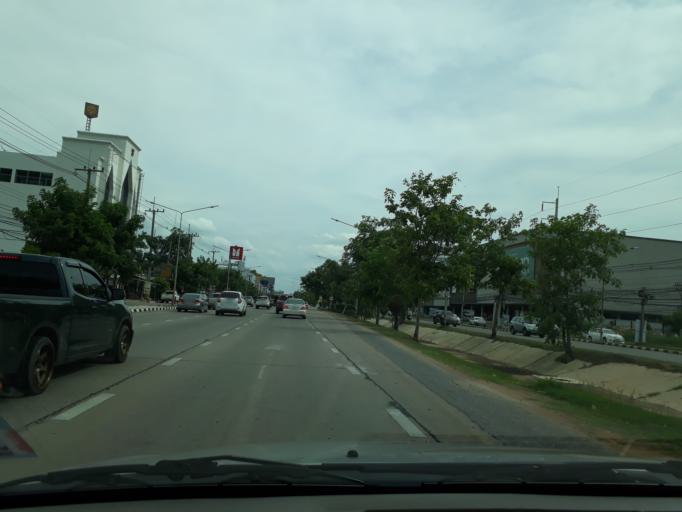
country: TH
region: Khon Kaen
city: Khon Kaen
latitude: 16.4268
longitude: 102.8223
